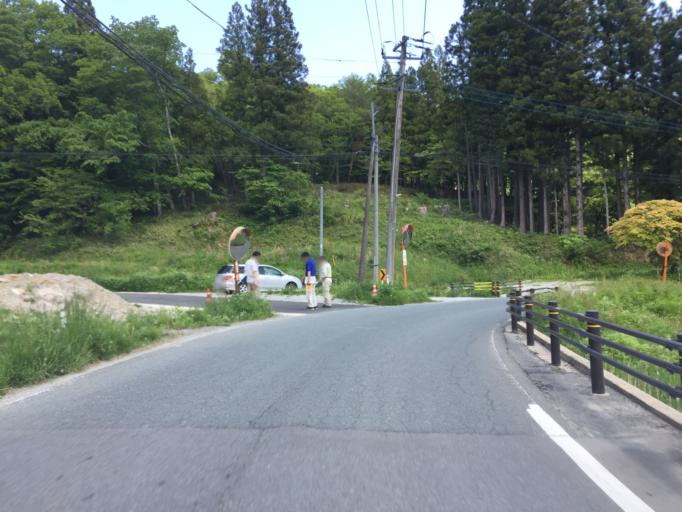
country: JP
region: Fukushima
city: Funehikimachi-funehiki
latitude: 37.5103
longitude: 140.7168
